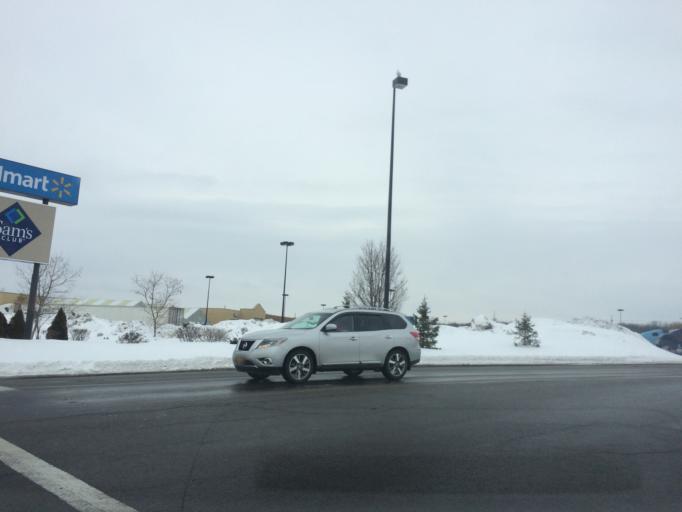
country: US
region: New York
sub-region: Monroe County
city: Rochester
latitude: 43.0794
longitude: -77.6250
